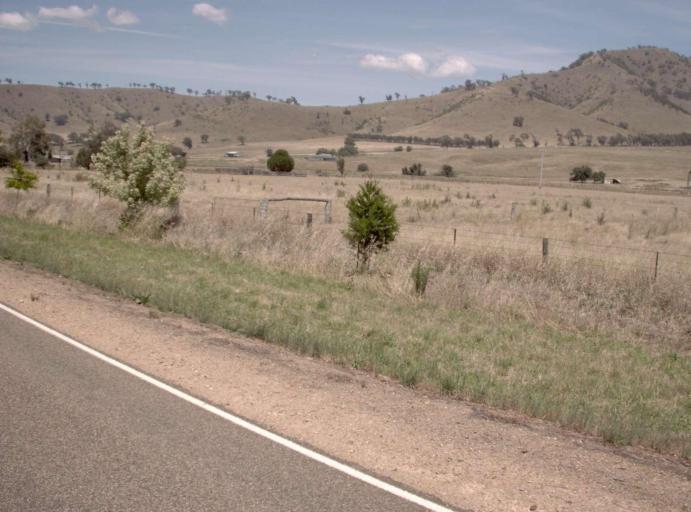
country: AU
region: Victoria
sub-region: East Gippsland
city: Bairnsdale
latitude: -37.2391
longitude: 147.7137
